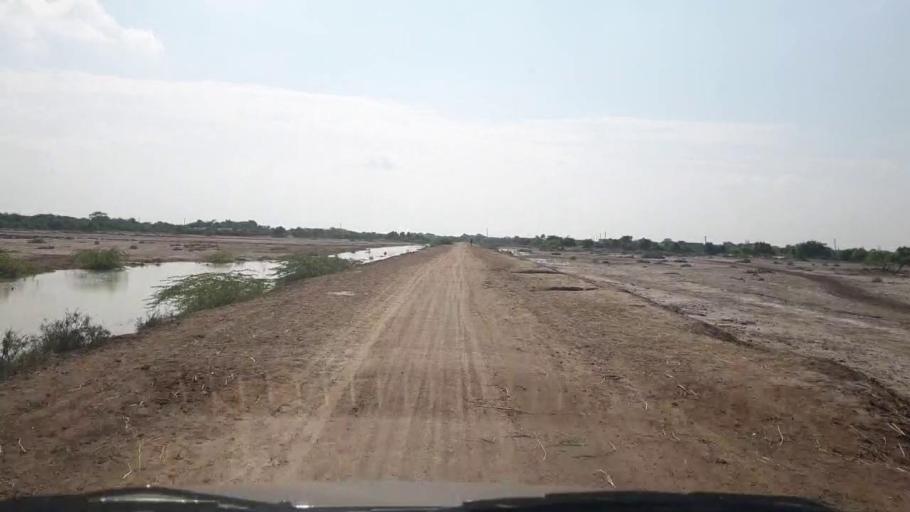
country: PK
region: Sindh
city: Badin
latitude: 24.4826
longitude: 68.6124
